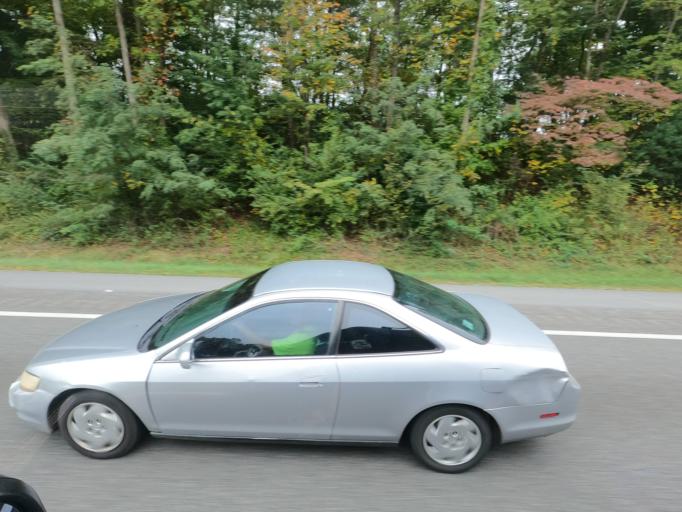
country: US
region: Tennessee
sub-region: Washington County
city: Johnson City
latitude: 36.3312
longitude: -82.3616
